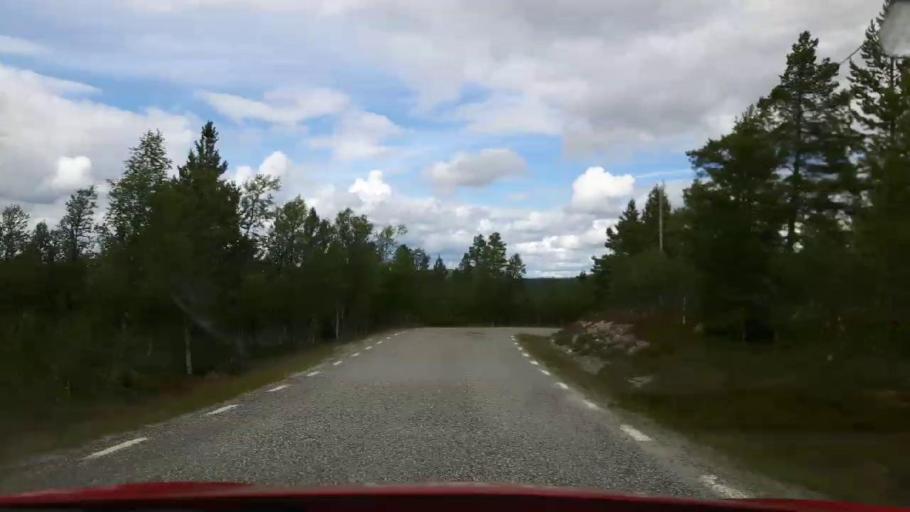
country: NO
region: Hedmark
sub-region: Engerdal
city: Engerdal
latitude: 62.3485
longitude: 12.7947
